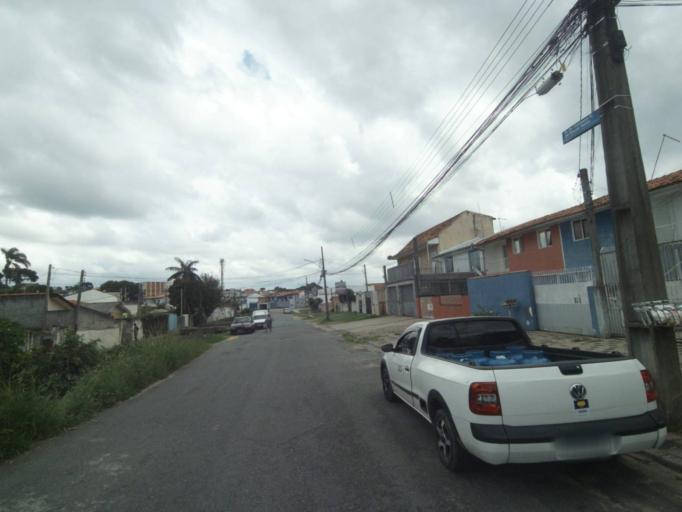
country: BR
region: Parana
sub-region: Pinhais
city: Pinhais
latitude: -25.4458
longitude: -49.2202
